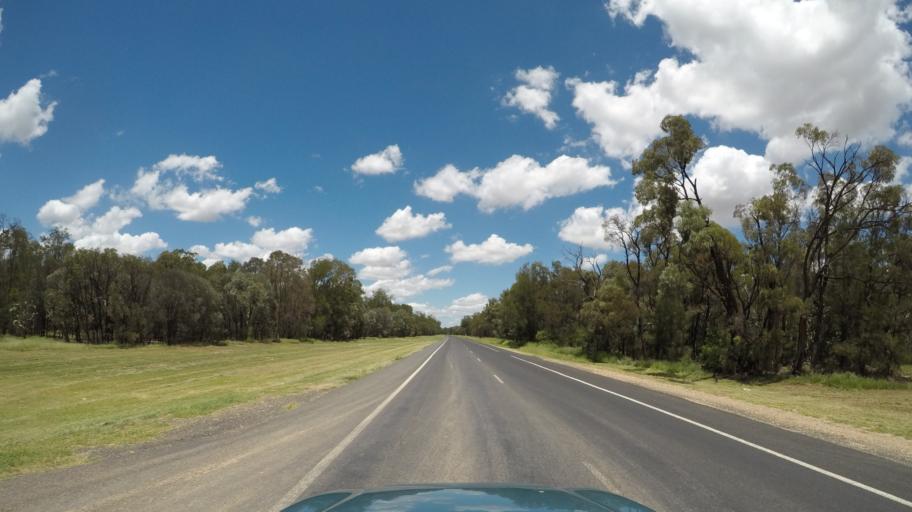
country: AU
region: Queensland
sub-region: Goondiwindi
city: Goondiwindi
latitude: -28.0837
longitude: 150.7364
